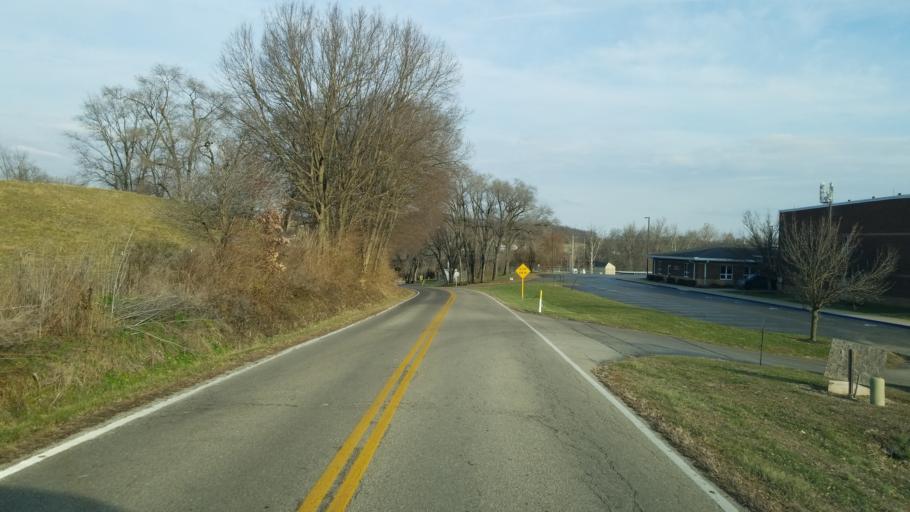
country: US
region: Ohio
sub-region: Ross County
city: Kingston
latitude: 39.4267
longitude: -82.9391
